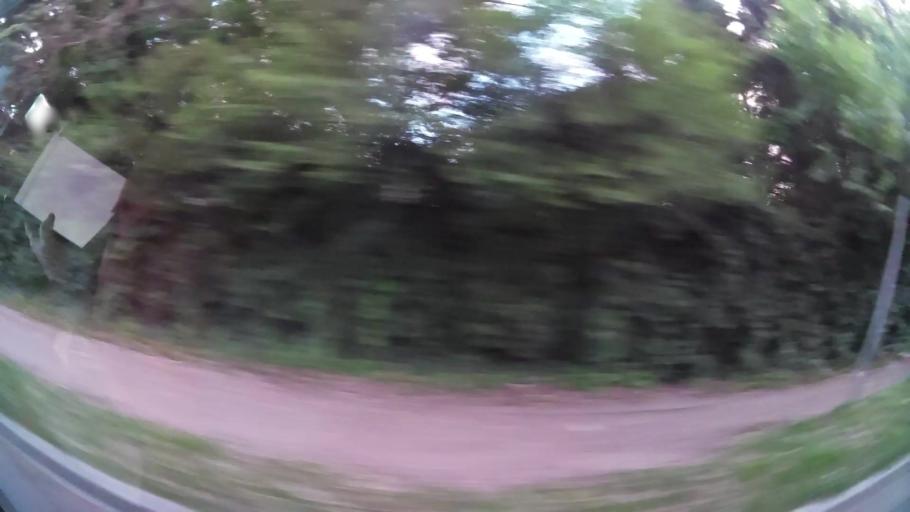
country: AR
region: Buenos Aires
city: Santa Catalina - Dique Lujan
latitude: -34.4801
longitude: -58.7731
